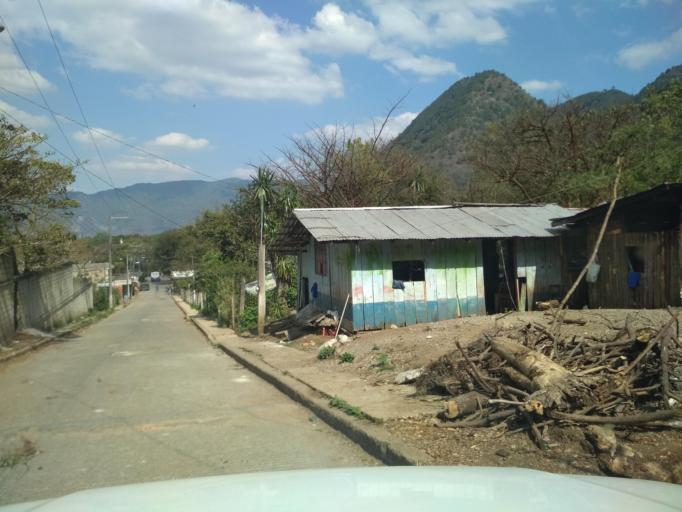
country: MX
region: Veracruz
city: Jalapilla
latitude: 18.8012
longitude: -97.1072
